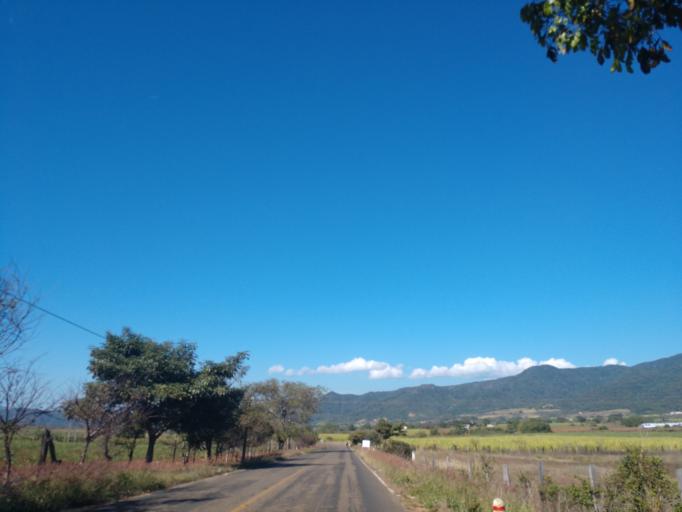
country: MX
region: Nayarit
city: Compostela
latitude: 21.2639
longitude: -104.8935
